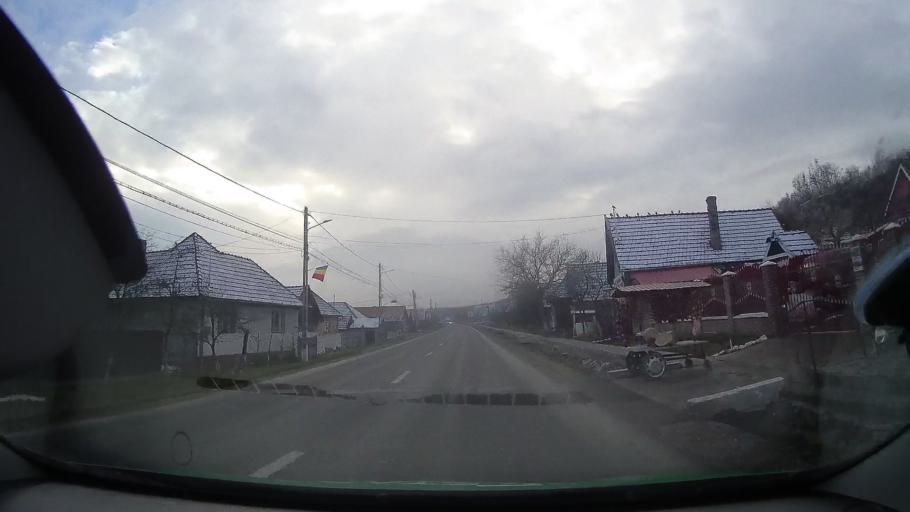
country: RO
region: Mures
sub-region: Comuna Cucerdea
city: Cucerdea
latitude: 46.3985
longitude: 24.2605
